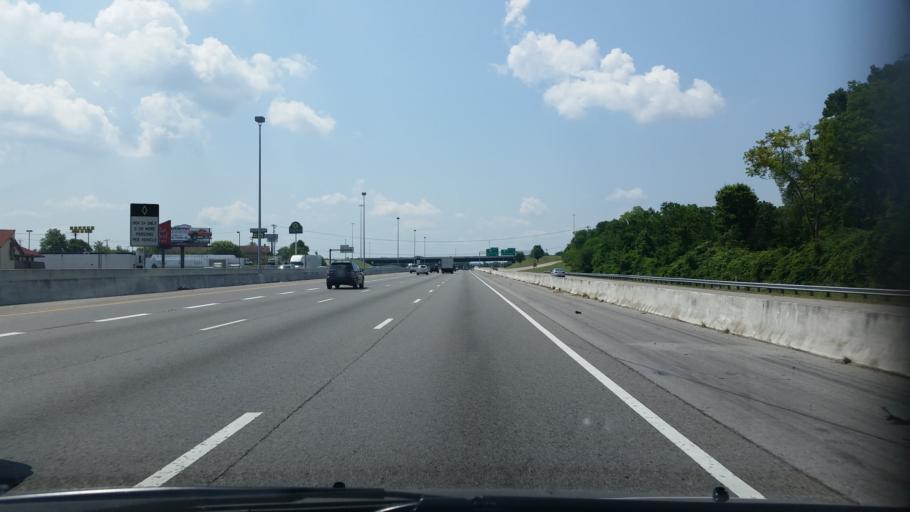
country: US
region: Tennessee
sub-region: Davidson County
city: Oak Hill
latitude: 36.0876
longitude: -86.7632
